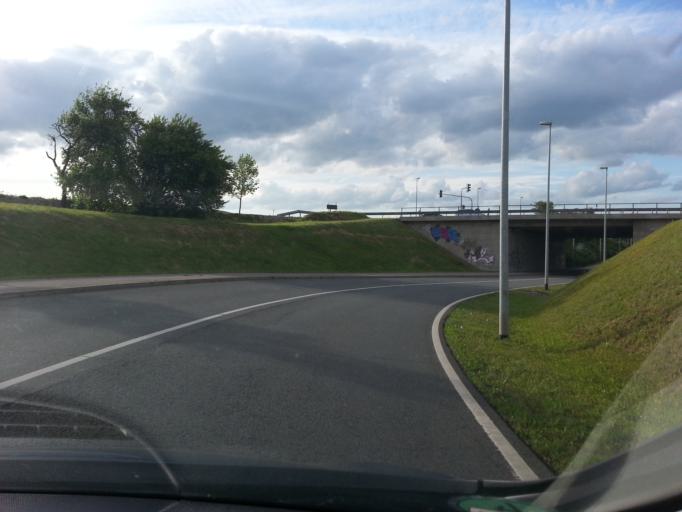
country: DE
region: Thuringia
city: Ingersleben
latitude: 50.9562
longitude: 10.9474
